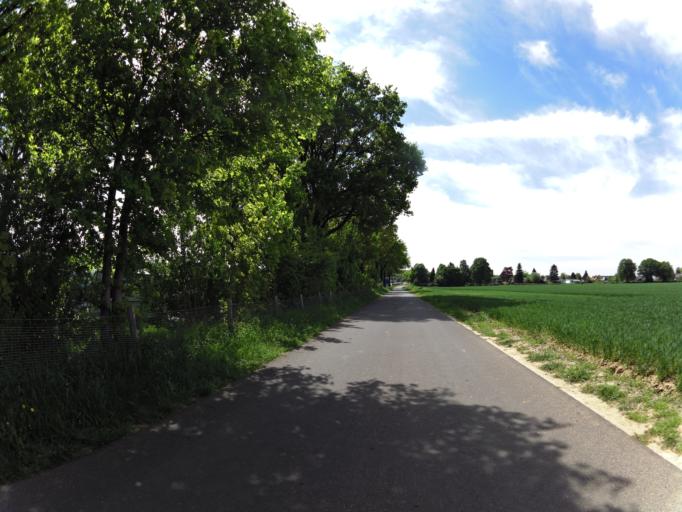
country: NL
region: Limburg
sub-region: Gemeente Simpelveld
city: Simpelveld
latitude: 50.8206
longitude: 5.9801
